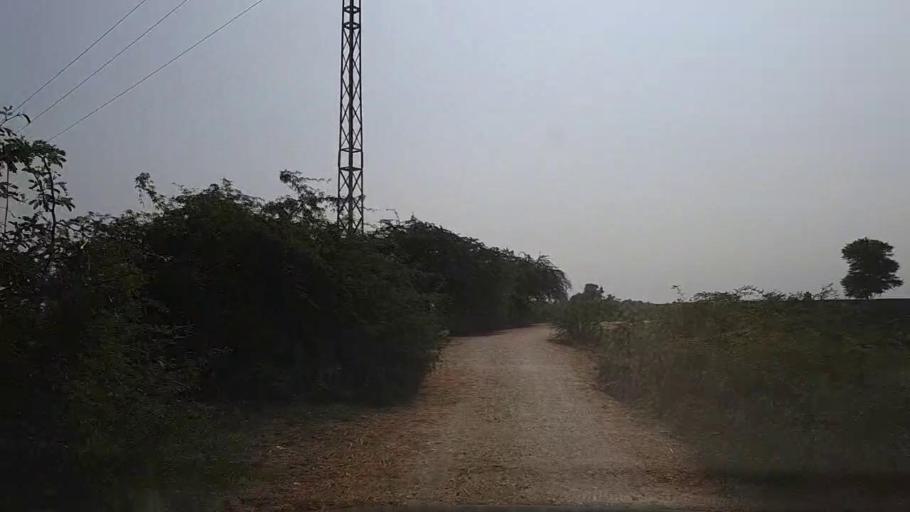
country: PK
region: Sindh
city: Chuhar Jamali
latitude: 24.5408
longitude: 67.9125
